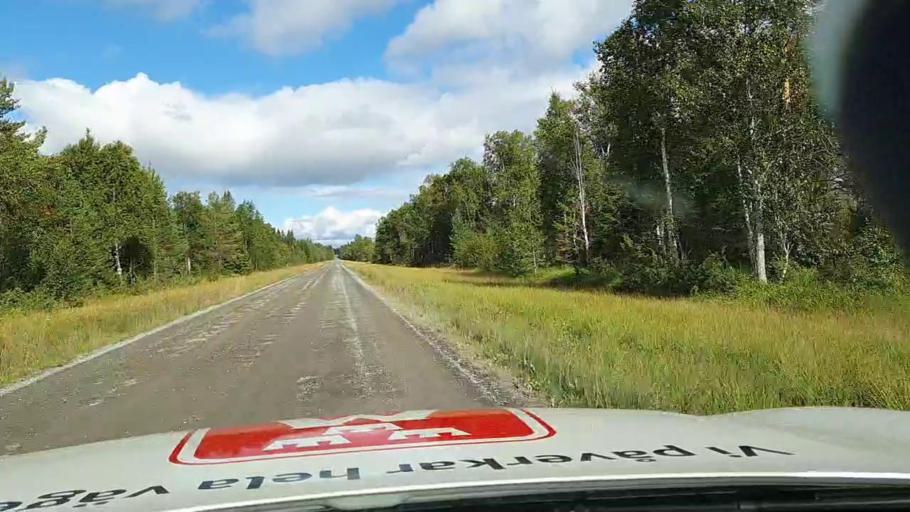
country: SE
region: Jaemtland
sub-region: Stroemsunds Kommun
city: Stroemsund
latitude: 63.7289
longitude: 15.2158
